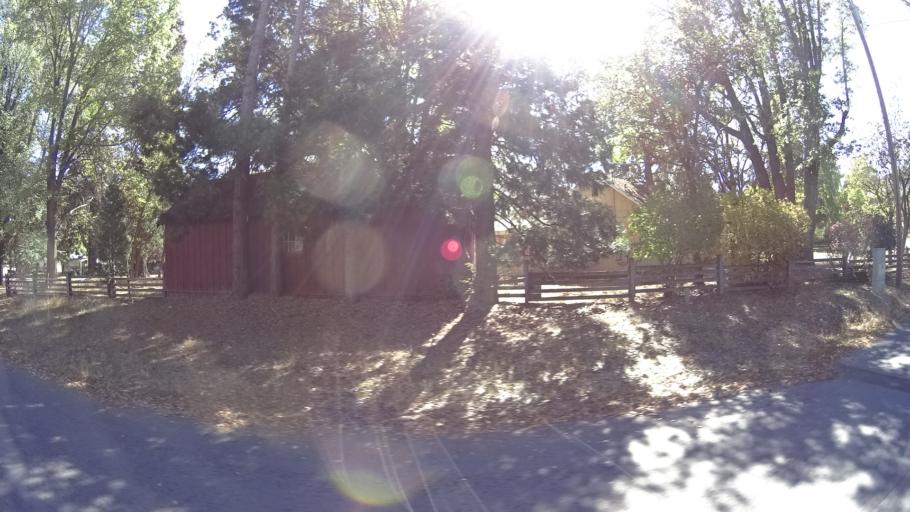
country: US
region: California
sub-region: Siskiyou County
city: Yreka
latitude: 41.4569
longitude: -122.8865
